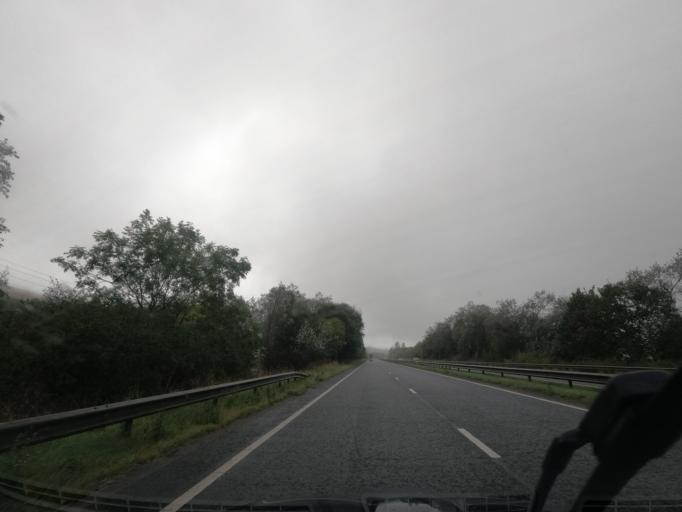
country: GB
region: England
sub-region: Redcar and Cleveland
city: South Bank
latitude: 54.5559
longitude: -1.1380
